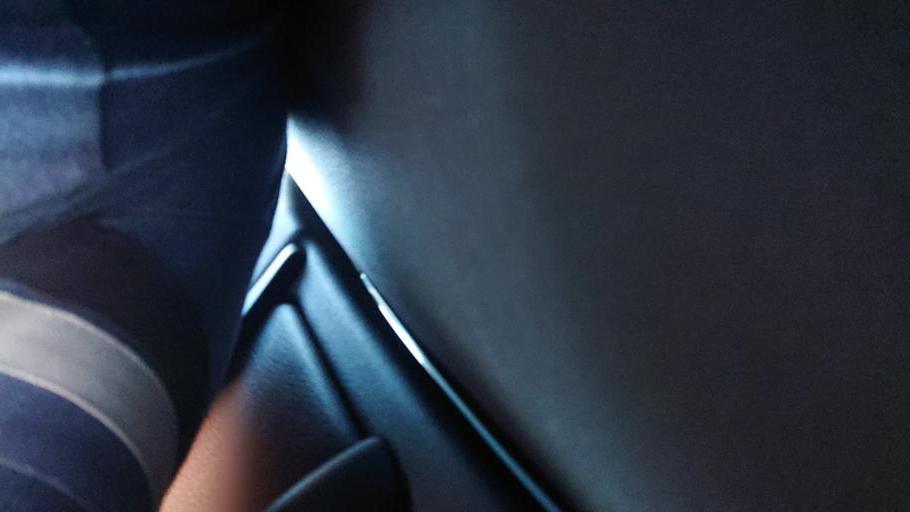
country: TW
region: Taiwan
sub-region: Tainan
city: Tainan
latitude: 23.0710
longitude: 120.2151
